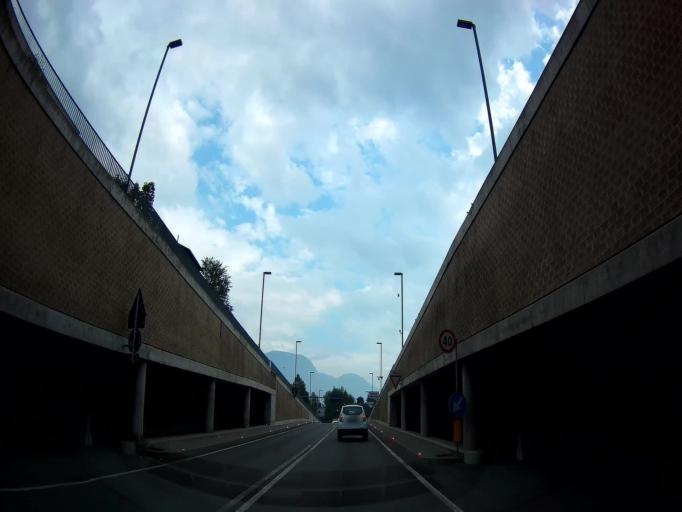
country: IT
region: Trentino-Alto Adige
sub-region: Bolzano
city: Merano
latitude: 46.6754
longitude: 11.1467
